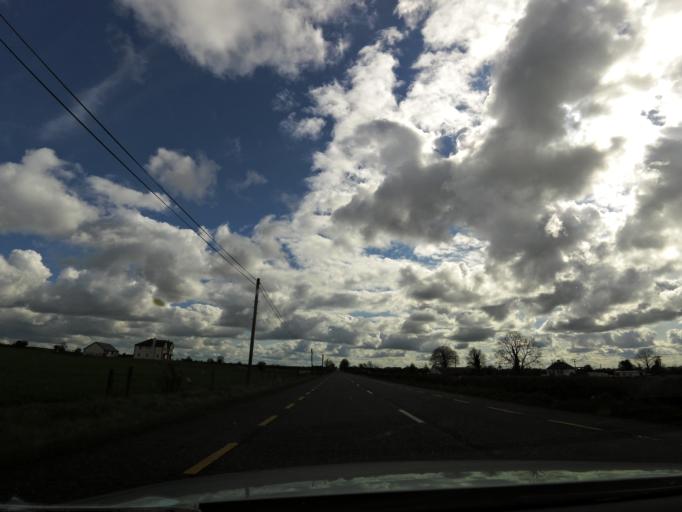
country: IE
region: Leinster
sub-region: Laois
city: Rathdowney
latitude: 52.7678
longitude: -7.5419
